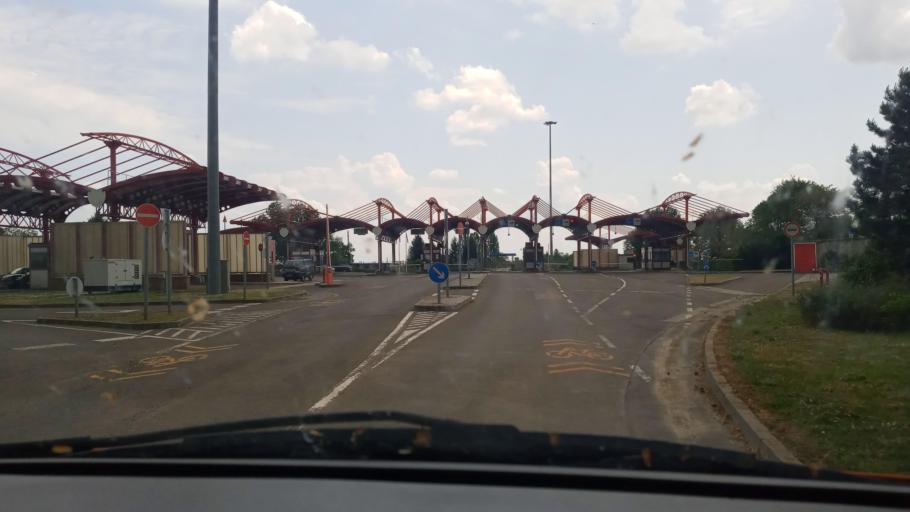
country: HU
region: Baranya
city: Beremend
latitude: 45.7685
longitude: 18.4523
